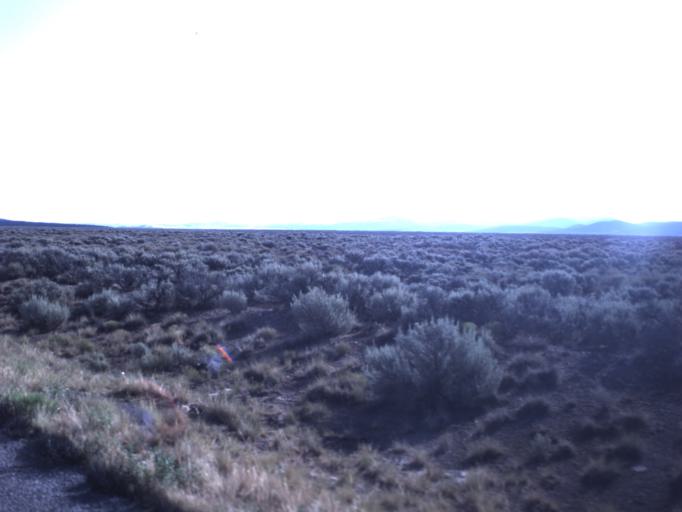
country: US
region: Utah
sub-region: Iron County
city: Enoch
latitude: 37.9894
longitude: -113.0012
